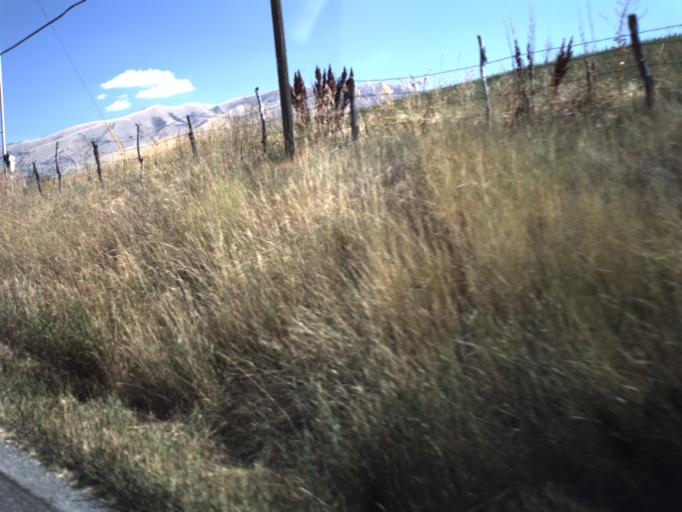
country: US
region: Utah
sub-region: Cache County
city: Hyrum
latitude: 41.5939
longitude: -111.8366
